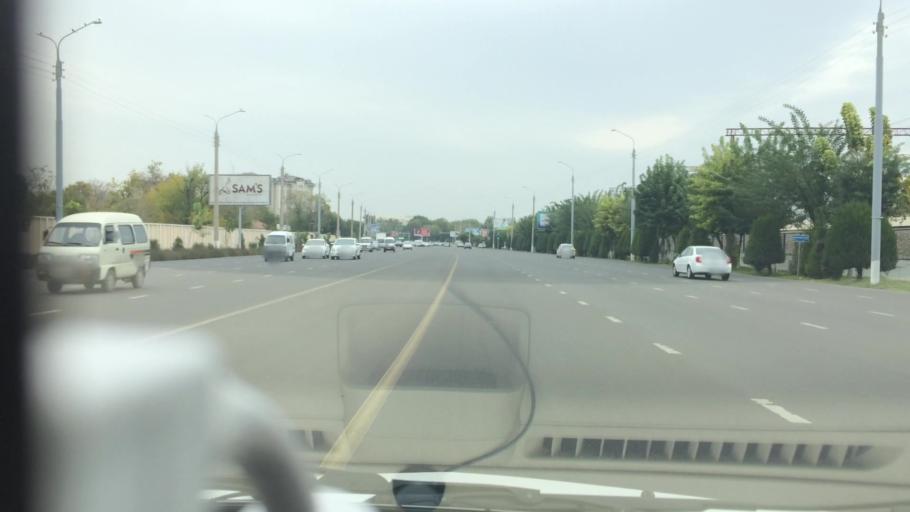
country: UZ
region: Toshkent Shahri
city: Tashkent
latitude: 41.2857
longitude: 69.2797
